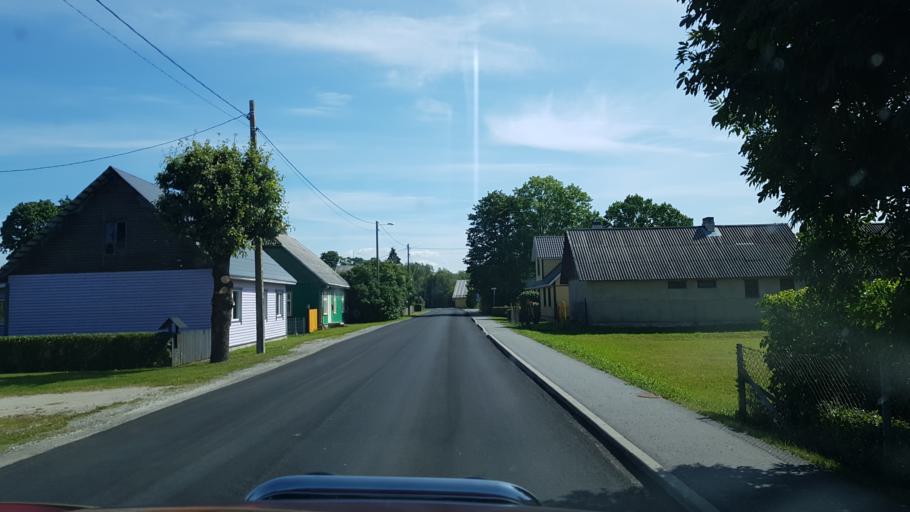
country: EE
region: Laeaene-Virumaa
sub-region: Tapa vald
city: Tapa
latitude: 59.1933
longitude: 25.8294
